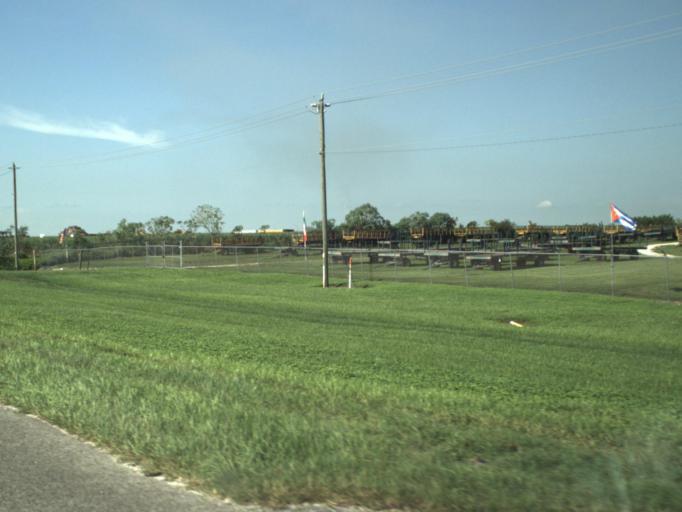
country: US
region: Florida
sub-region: Palm Beach County
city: South Bay
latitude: 26.6209
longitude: -80.7121
